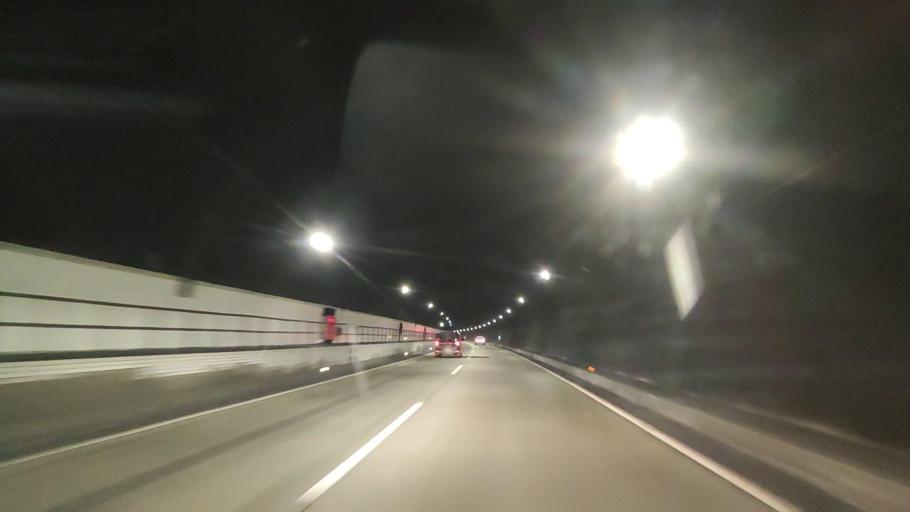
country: JP
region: Okayama
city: Kamogatacho-kamogata
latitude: 34.5562
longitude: 133.6123
